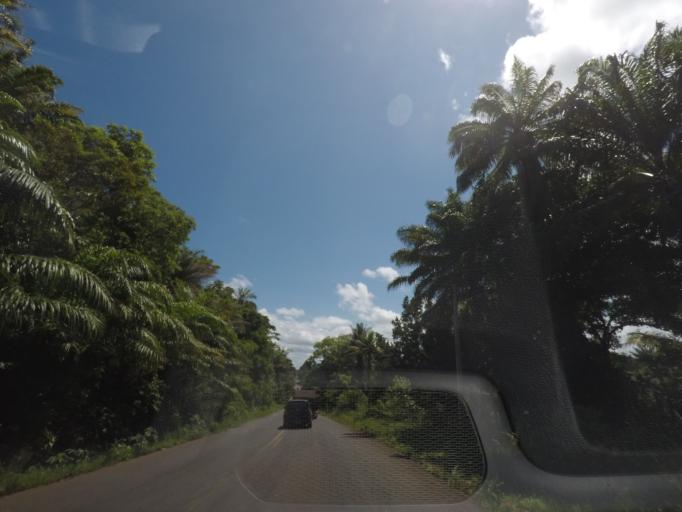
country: BR
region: Bahia
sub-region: Valenca
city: Valenca
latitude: -13.4470
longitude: -39.0847
